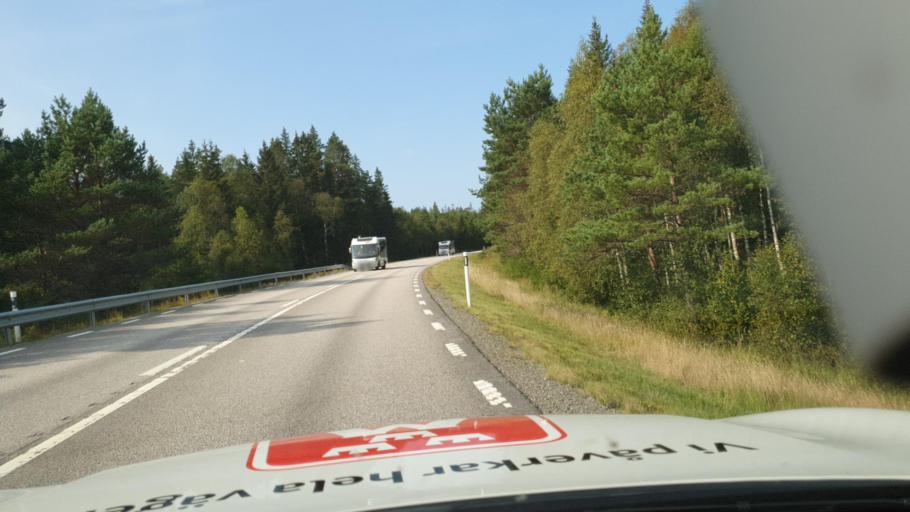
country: SE
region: Vaestra Goetaland
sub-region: Dals-Ed Kommun
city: Ed
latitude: 58.8430
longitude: 11.7478
